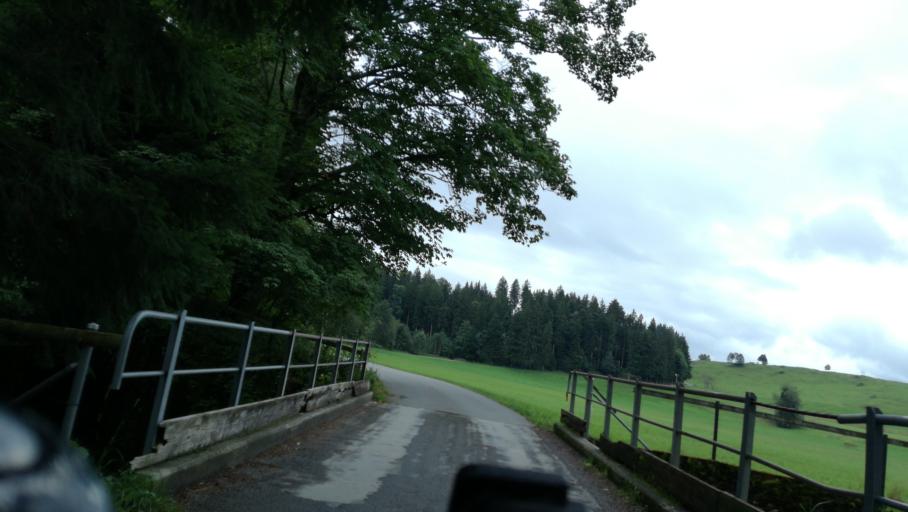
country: CH
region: Zug
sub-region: Zug
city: Zug
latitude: 47.1375
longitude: 8.5331
